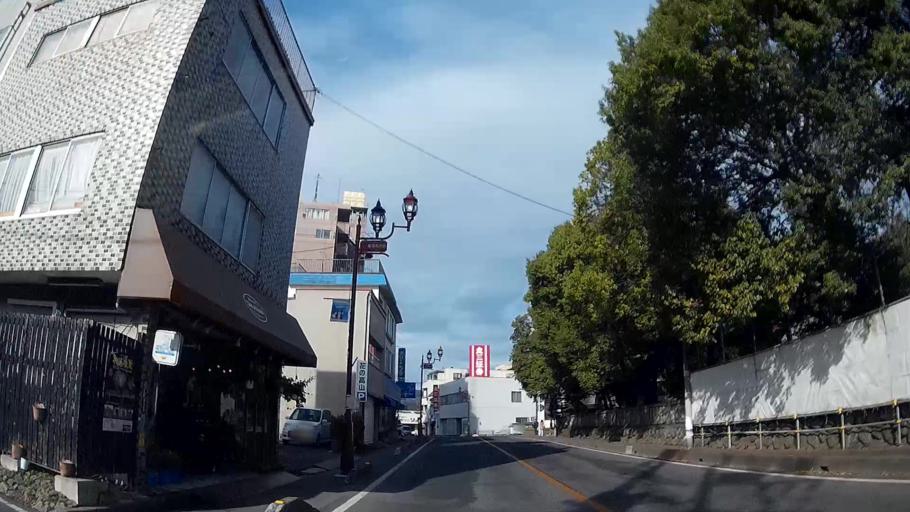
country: JP
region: Saitama
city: Chichibu
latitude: 35.9966
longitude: 139.0840
